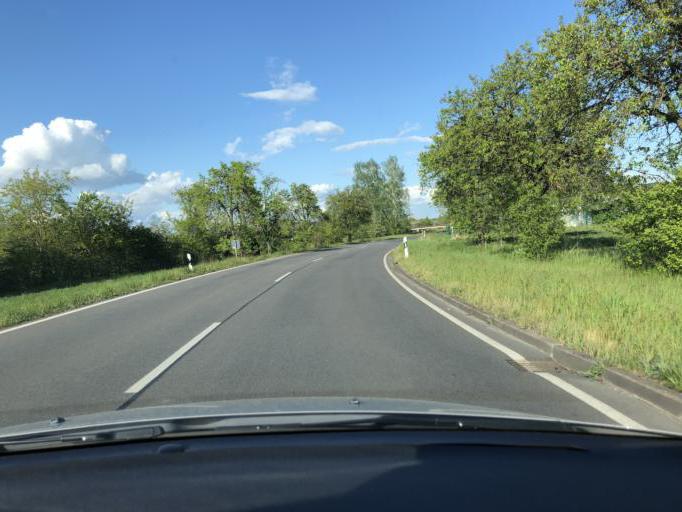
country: DE
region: Saxony
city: Deutzen
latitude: 51.1165
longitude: 12.4311
